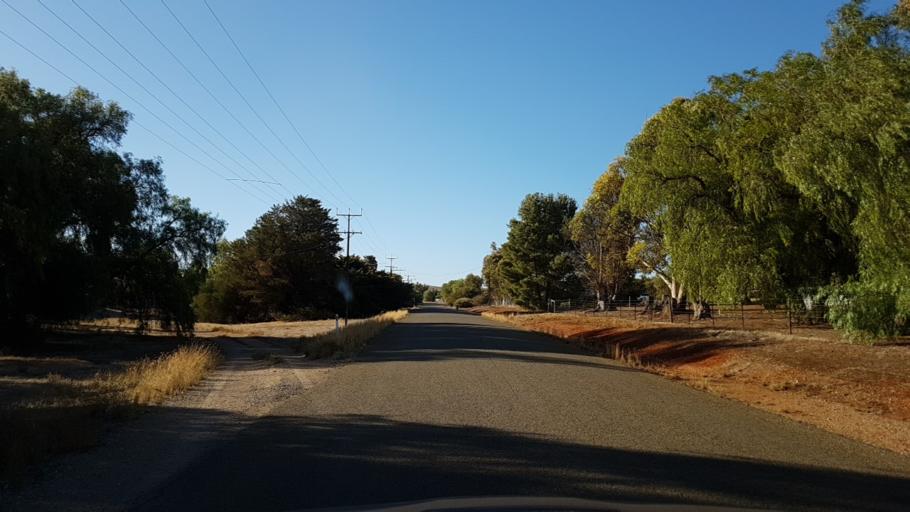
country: AU
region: South Australia
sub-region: Clare and Gilbert Valleys
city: Clare
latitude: -33.6698
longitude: 138.9318
